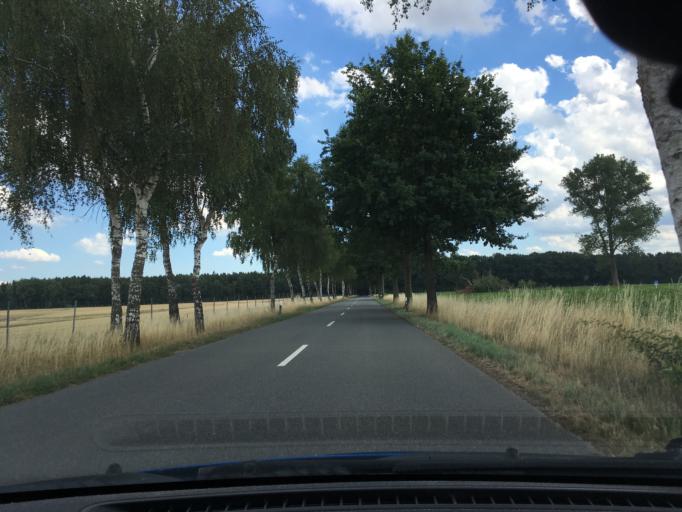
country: DE
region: Lower Saxony
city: Wriedel
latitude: 53.0511
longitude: 10.2517
